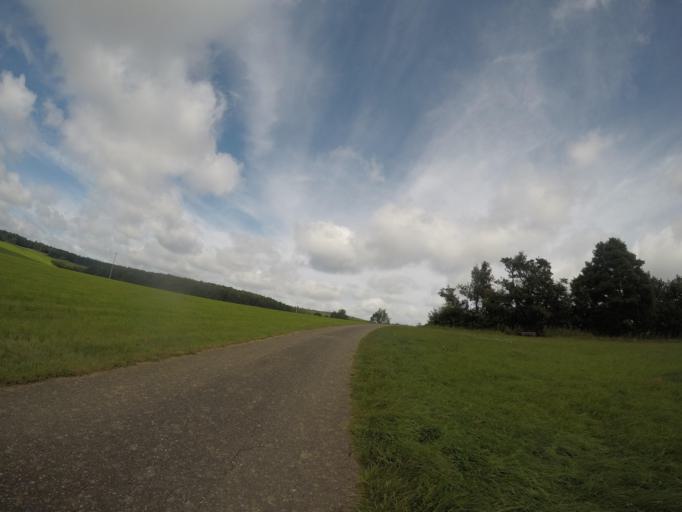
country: DE
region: Baden-Wuerttemberg
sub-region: Tuebingen Region
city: Westerheim
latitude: 48.4561
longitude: 9.6345
